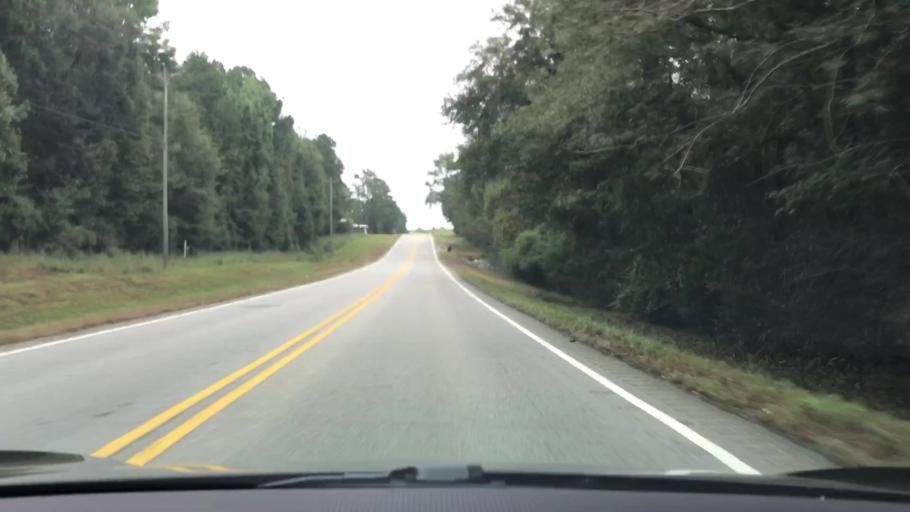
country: US
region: Alabama
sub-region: Pike County
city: Troy
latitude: 31.6560
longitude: -85.9647
